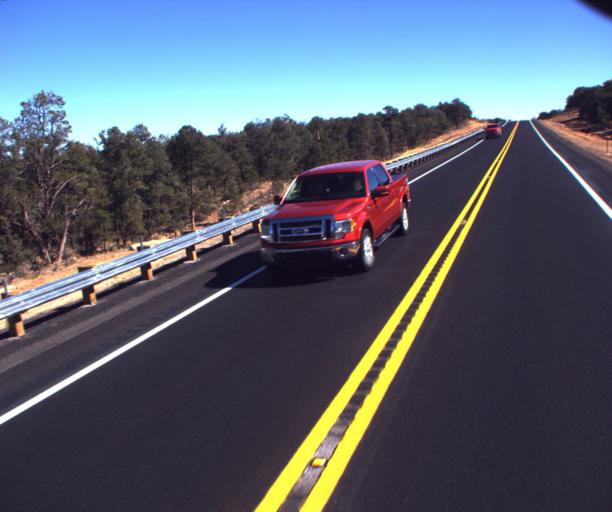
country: US
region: Arizona
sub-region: Apache County
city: Ganado
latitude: 35.7138
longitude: -109.3352
